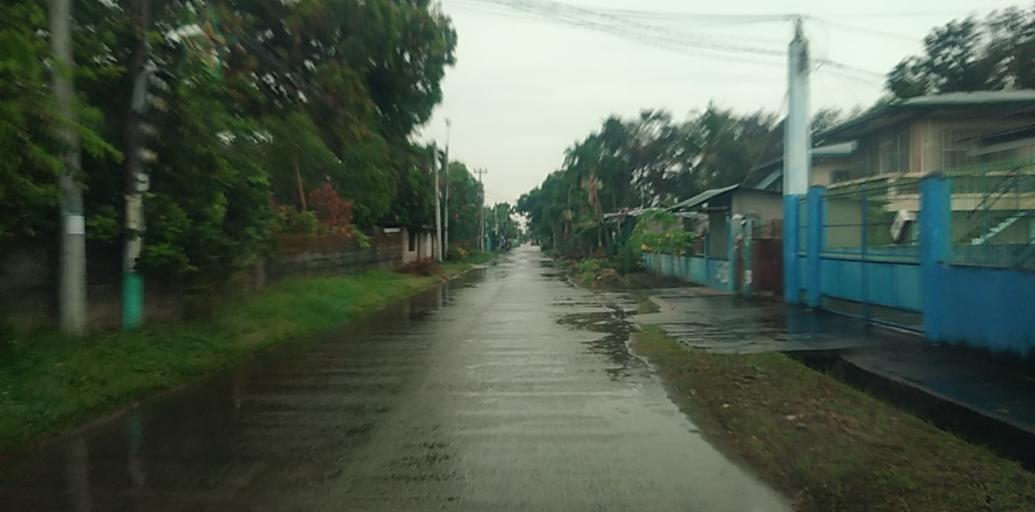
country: PH
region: Central Luzon
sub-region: Province of Pampanga
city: Arenas
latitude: 15.1687
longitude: 120.6865
